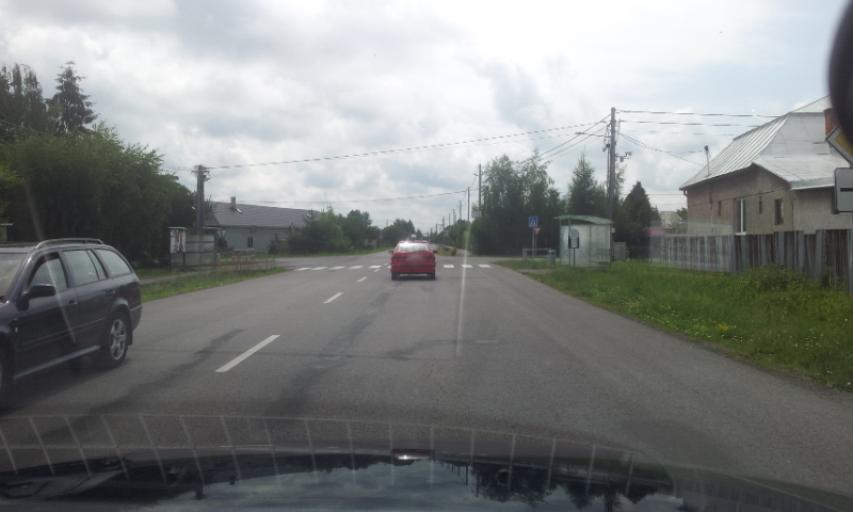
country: SK
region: Kosicky
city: Michalovce
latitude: 48.6930
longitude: 21.9773
